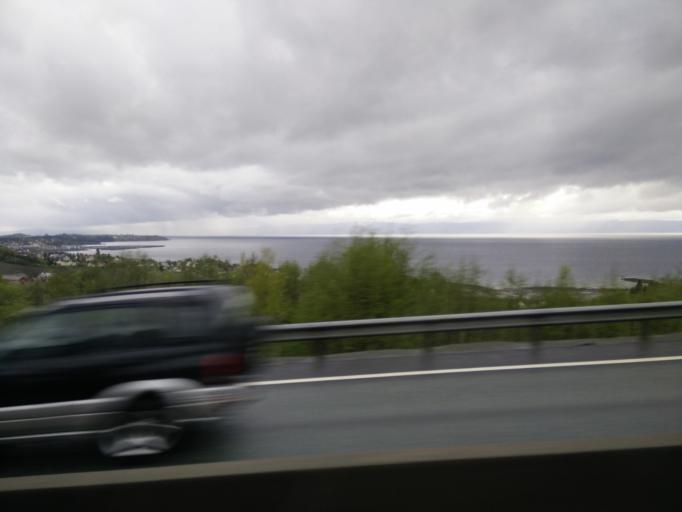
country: NO
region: Sor-Trondelag
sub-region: Malvik
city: Malvik
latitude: 63.4243
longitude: 10.5628
